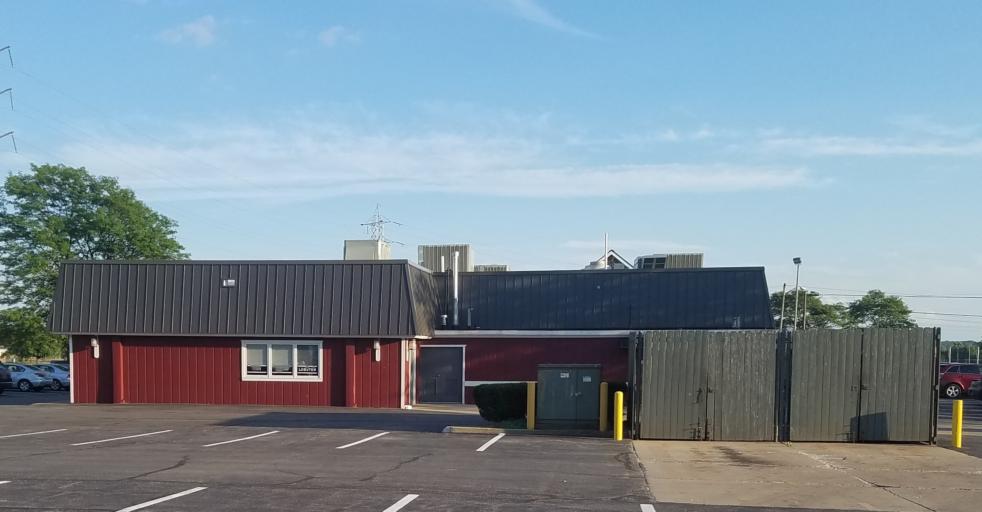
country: US
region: Ohio
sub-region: Richland County
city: Ontario
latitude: 40.7748
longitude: -82.5987
